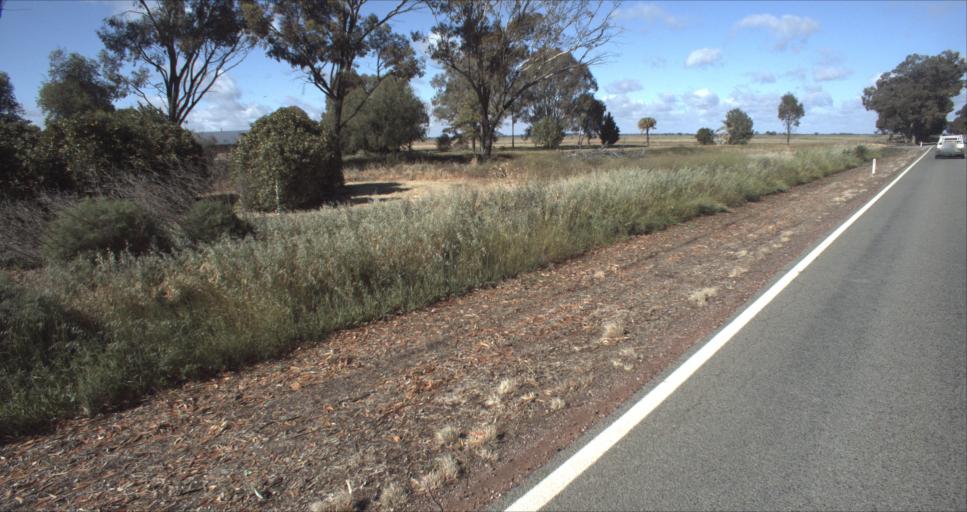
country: AU
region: New South Wales
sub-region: Leeton
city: Leeton
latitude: -34.5455
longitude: 146.3280
